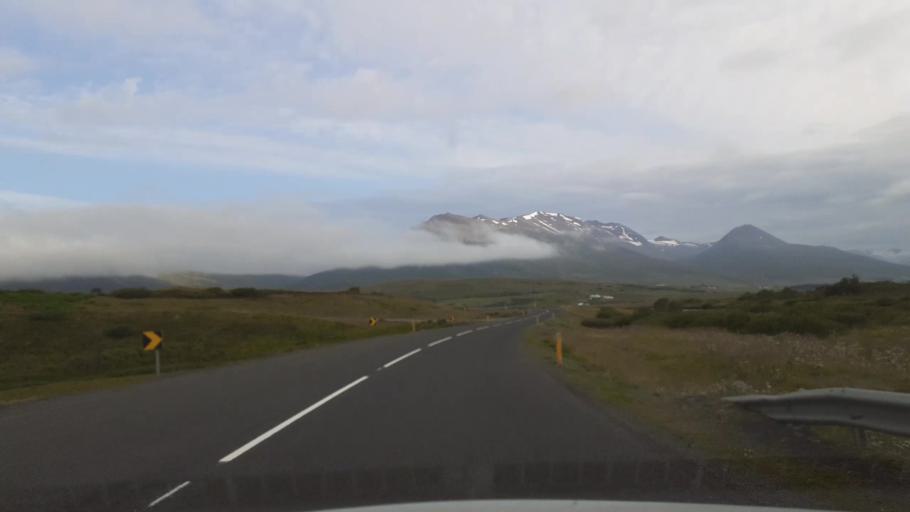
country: IS
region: Northeast
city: Dalvik
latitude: 65.9595
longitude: -18.5378
